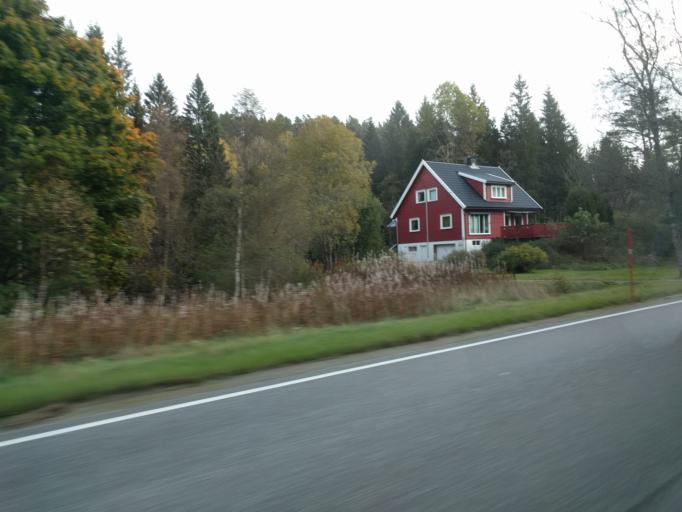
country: NO
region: Vest-Agder
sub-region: Kristiansand
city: Strai
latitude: 58.2537
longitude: 7.8582
